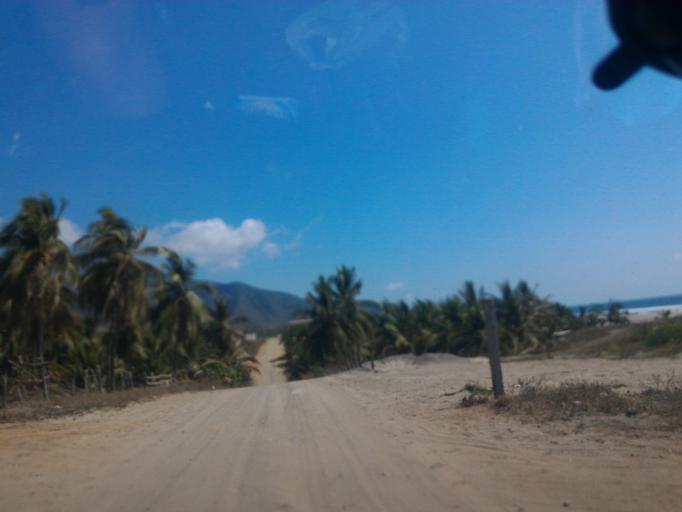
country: MX
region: Michoacan
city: Coahuayana Viejo
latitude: 18.5904
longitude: -103.6864
